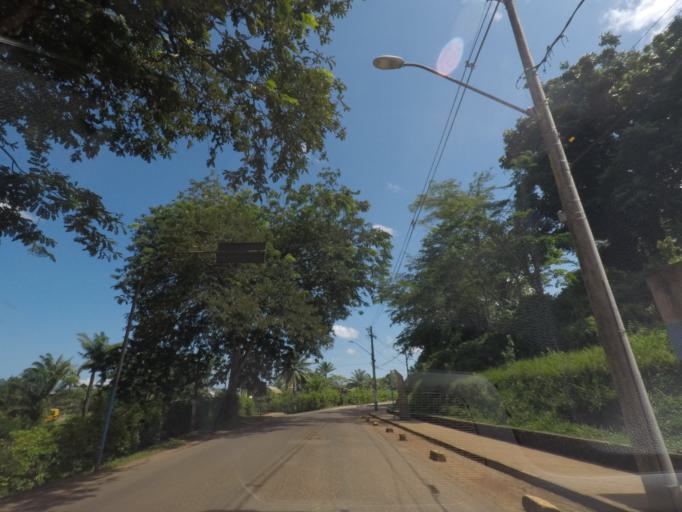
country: BR
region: Bahia
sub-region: Taperoa
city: Taperoa
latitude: -13.5337
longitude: -39.1006
